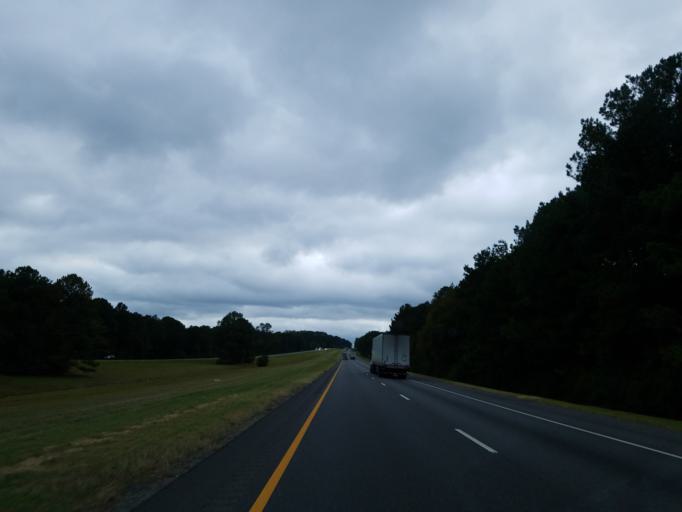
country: US
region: Alabama
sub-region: Hale County
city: Moundville
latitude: 32.9986
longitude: -87.7729
